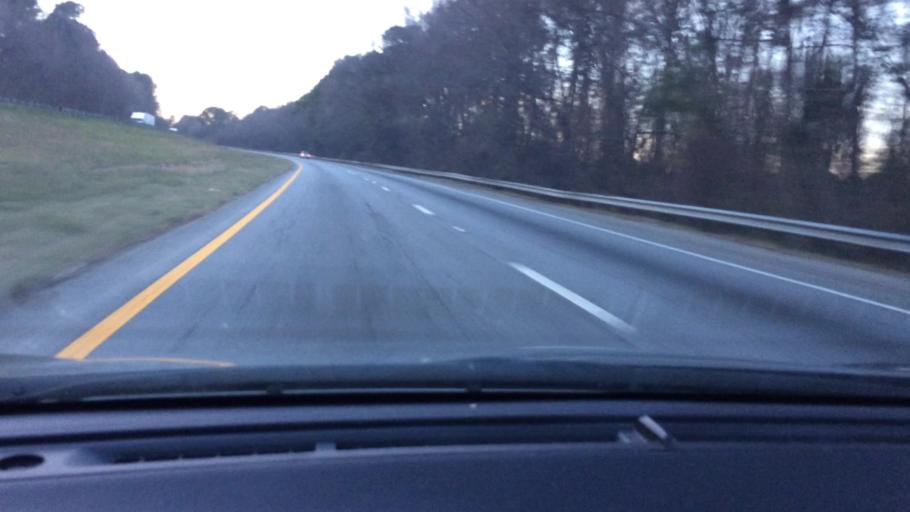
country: US
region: South Carolina
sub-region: Laurens County
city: Joanna
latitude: 34.4239
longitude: -81.7192
